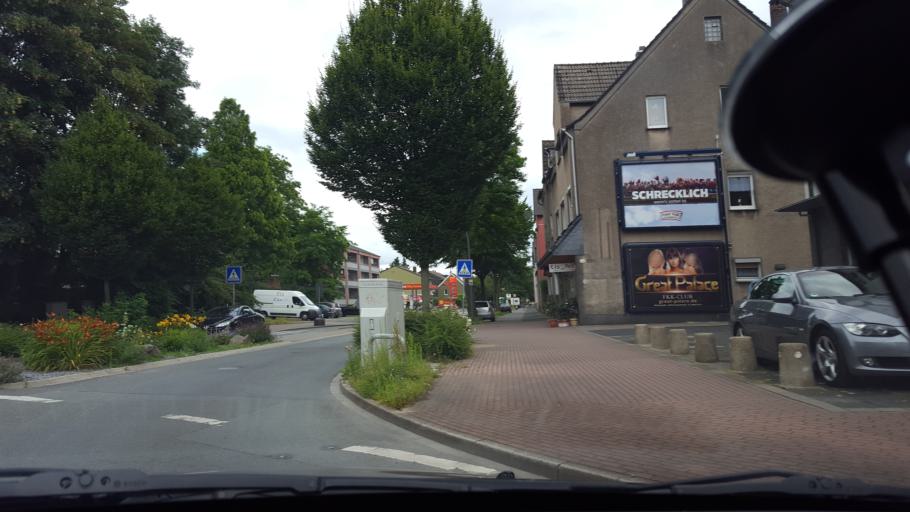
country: DE
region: North Rhine-Westphalia
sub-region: Regierungsbezirk Munster
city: Recklinghausen
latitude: 51.6216
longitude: 7.2276
